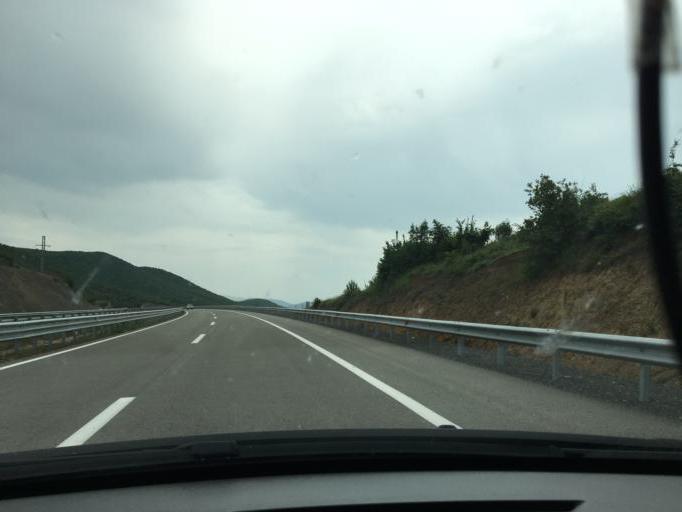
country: MK
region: Gevgelija
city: Miravci
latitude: 41.3376
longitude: 22.3823
